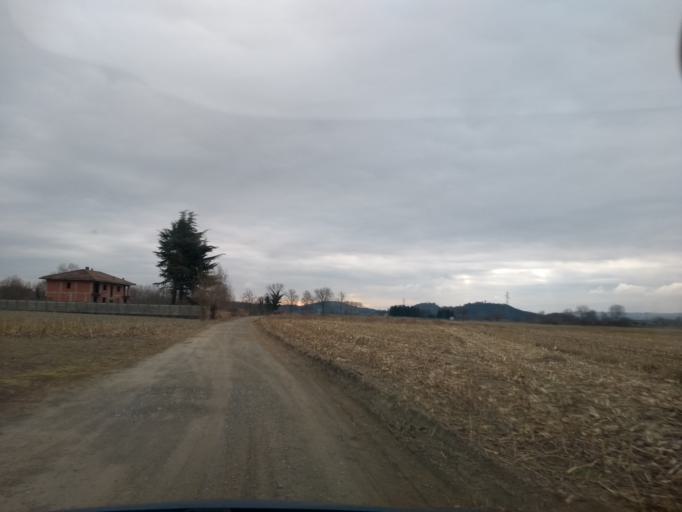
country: IT
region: Piedmont
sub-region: Provincia di Torino
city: Fiorano Canavese
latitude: 45.4822
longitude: 7.8417
